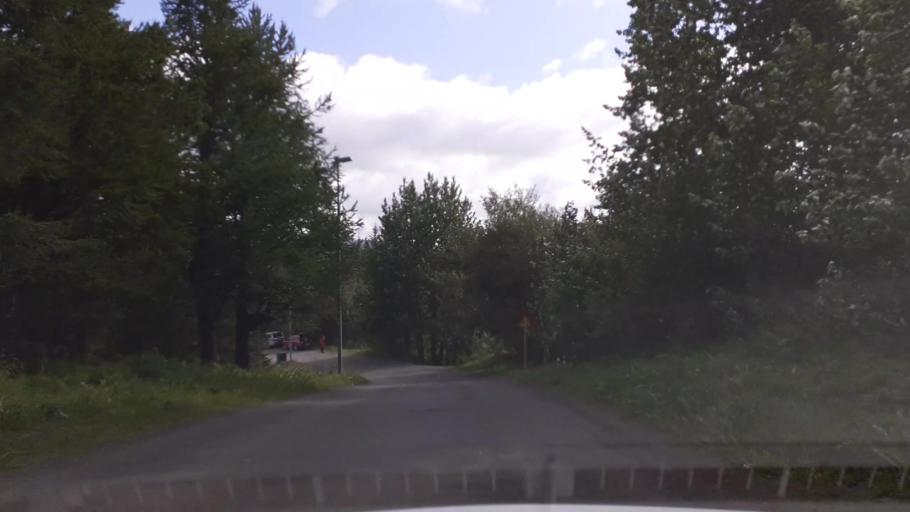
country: IS
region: Northeast
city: Akureyri
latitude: 65.6473
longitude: -18.0871
